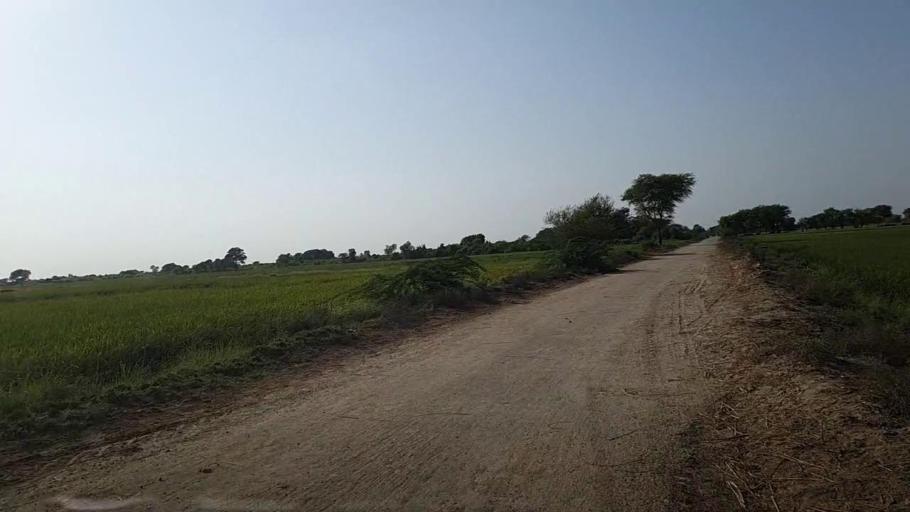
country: PK
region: Sindh
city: Kario
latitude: 24.8166
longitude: 68.4990
